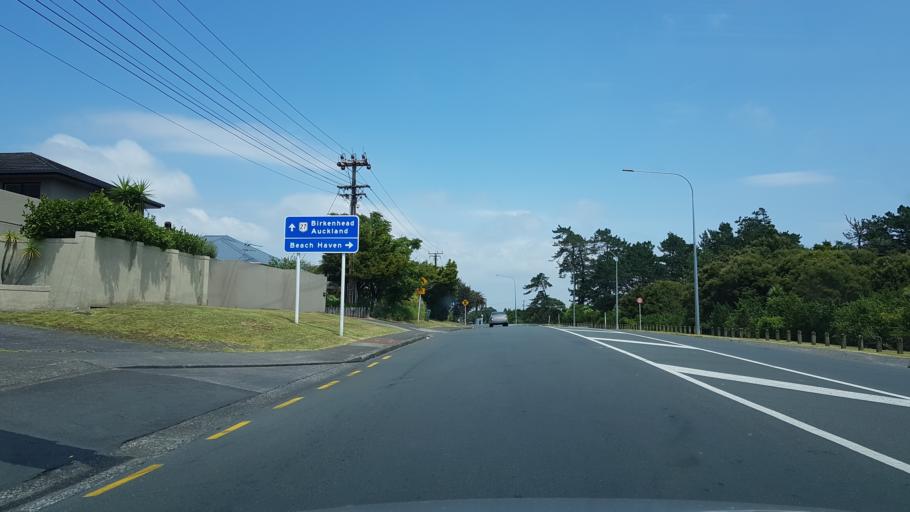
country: NZ
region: Auckland
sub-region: Auckland
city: North Shore
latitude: -36.7965
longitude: 174.7236
